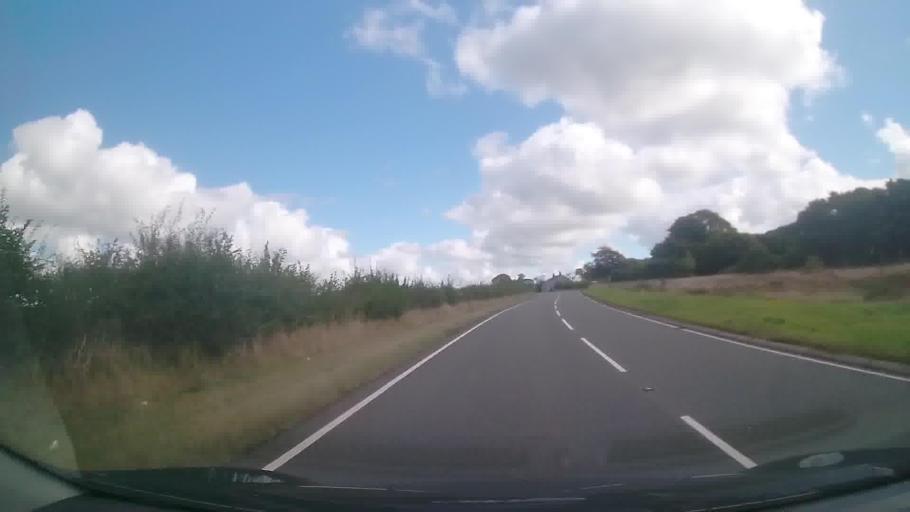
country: GB
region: Wales
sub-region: Pembrokeshire
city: Pembroke
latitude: 51.6870
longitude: -4.8762
